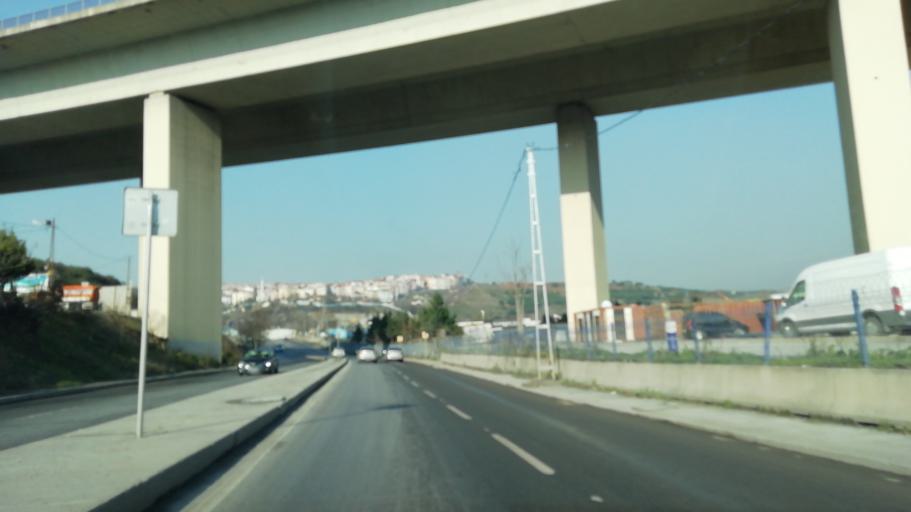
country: TR
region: Istanbul
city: Sultangazi
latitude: 41.0939
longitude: 28.9216
